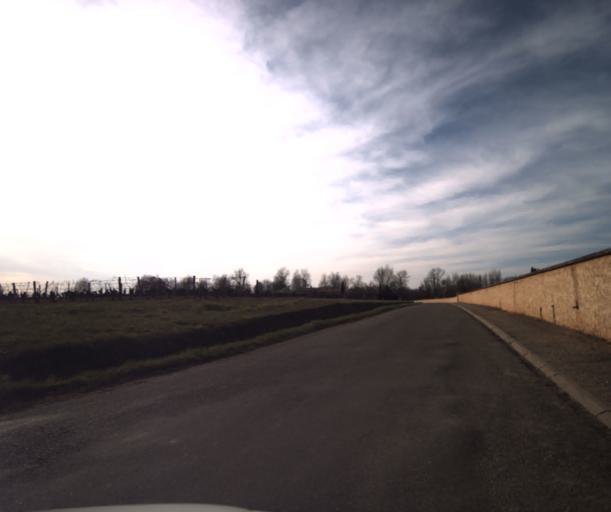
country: FR
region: Midi-Pyrenees
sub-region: Departement du Tarn-et-Garonne
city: Labastide-Saint-Pierre
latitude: 43.9156
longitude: 1.3621
